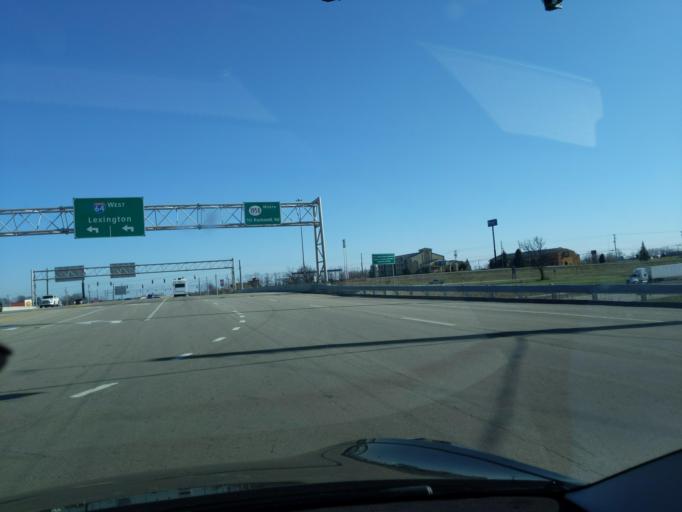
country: US
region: Kentucky
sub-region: Clark County
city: Winchester
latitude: 38.0103
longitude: -84.2089
